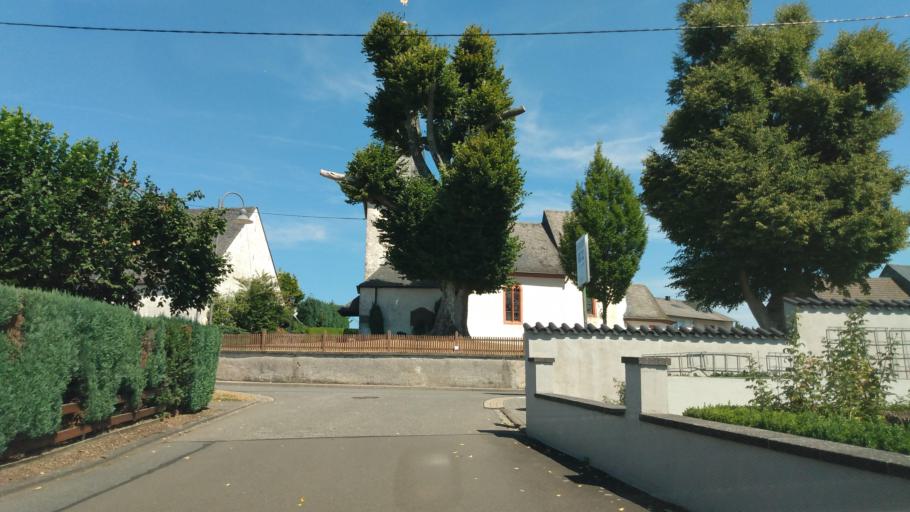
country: DE
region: Rheinland-Pfalz
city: Morbach
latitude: 49.8303
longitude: 7.0836
